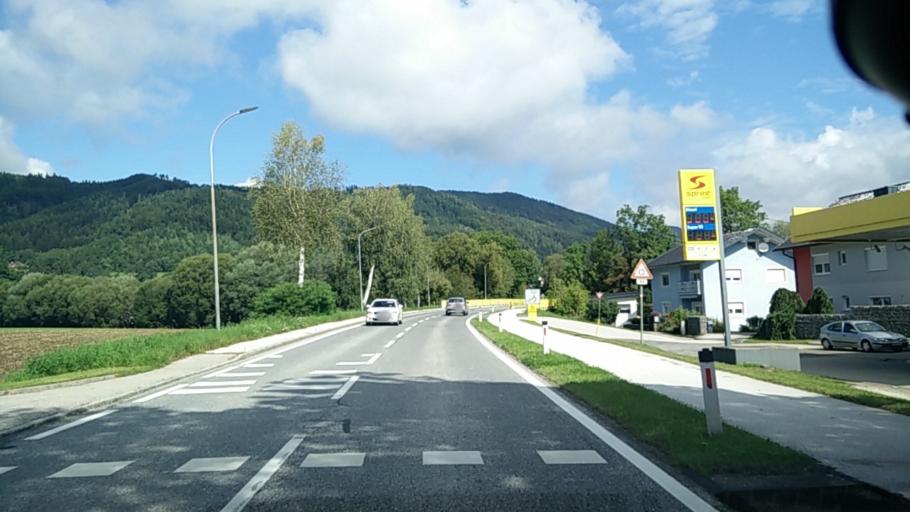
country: AT
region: Carinthia
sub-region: Politischer Bezirk Sankt Veit an der Glan
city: Bruckl
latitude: 46.7465
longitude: 14.5313
